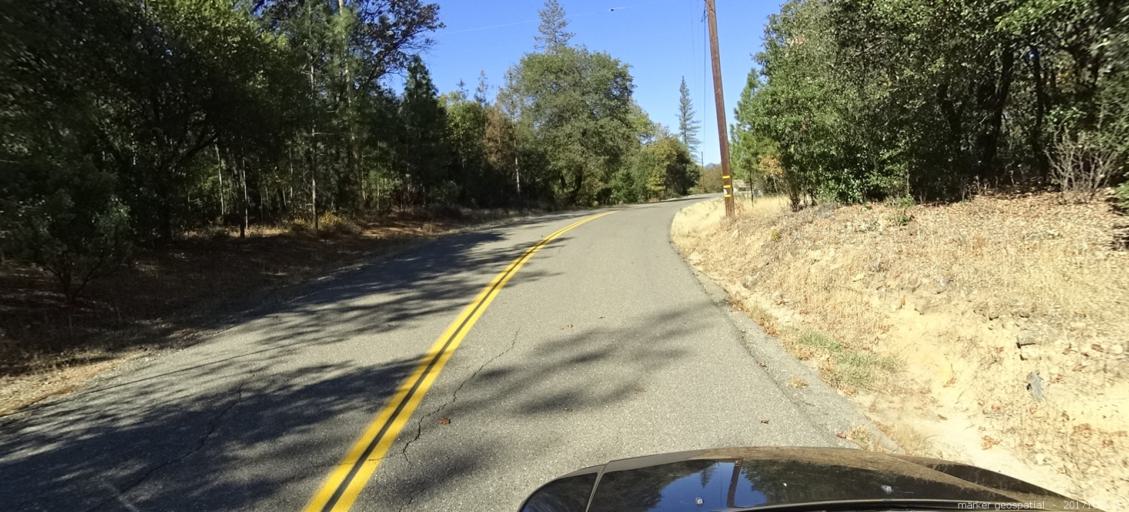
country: US
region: California
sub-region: Shasta County
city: Shasta
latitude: 40.5872
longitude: -122.5413
